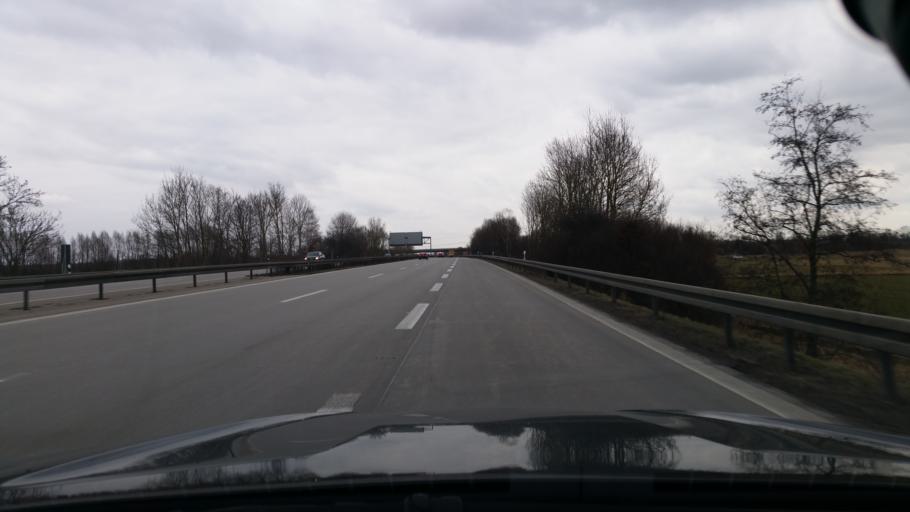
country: DE
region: Bavaria
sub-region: Upper Bavaria
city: Langenbach
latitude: 48.3975
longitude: 11.8607
